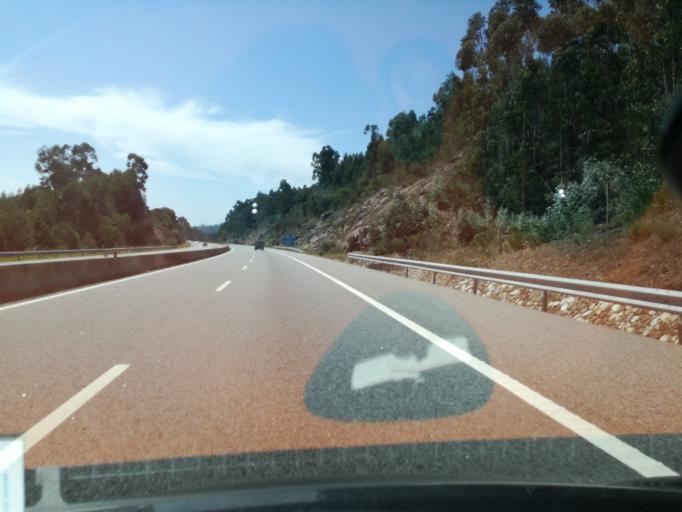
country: PT
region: Viana do Castelo
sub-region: Viana do Castelo
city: Meadela
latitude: 41.7622
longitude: -8.7941
